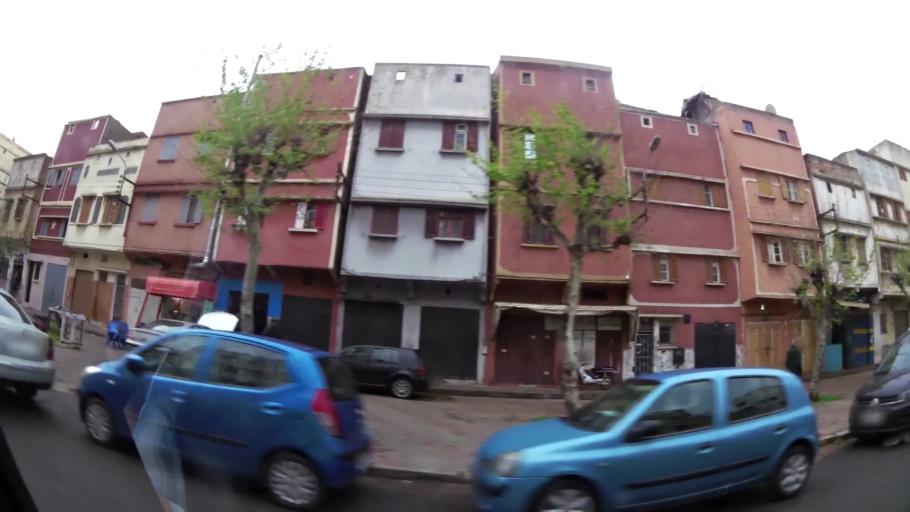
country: MA
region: Grand Casablanca
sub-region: Casablanca
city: Casablanca
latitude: 33.5552
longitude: -7.5851
